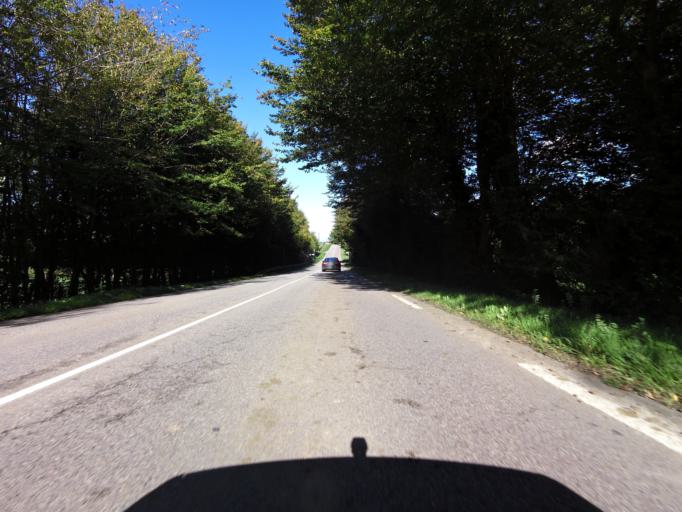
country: FR
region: Lower Normandy
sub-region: Departement de l'Orne
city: Vimoutiers
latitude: 48.9422
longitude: 0.1964
